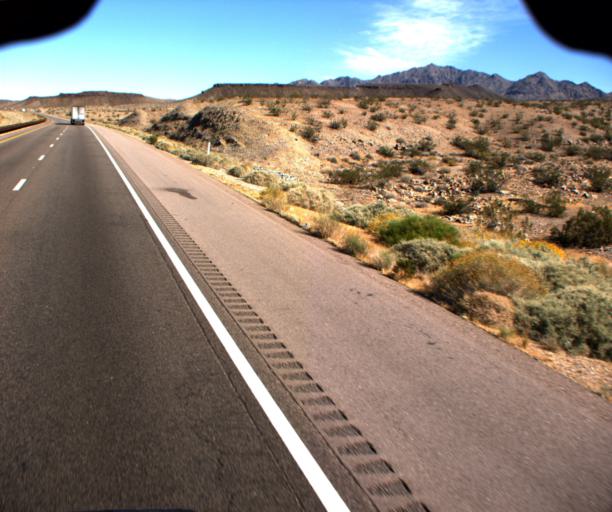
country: US
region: Nevada
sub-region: Clark County
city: Boulder City
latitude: 35.9276
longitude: -114.6337
